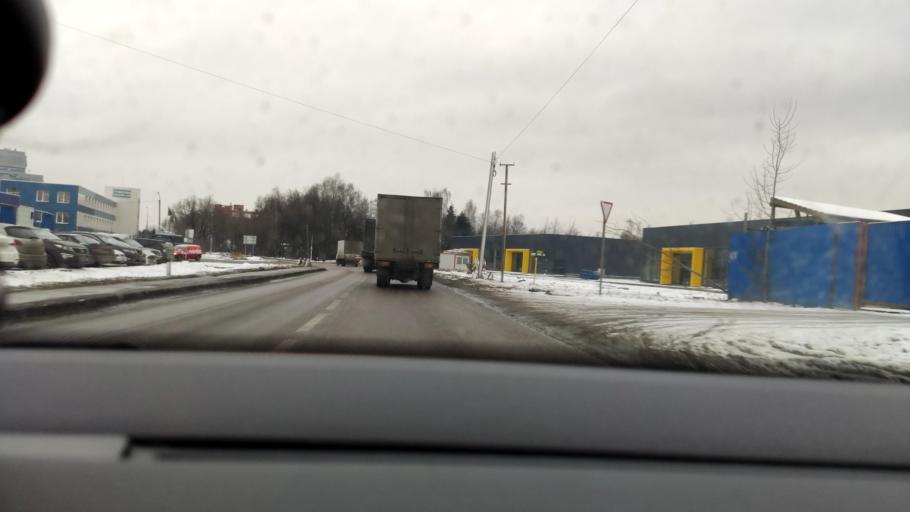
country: RU
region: Moscow
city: Khimki
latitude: 55.9197
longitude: 37.4209
